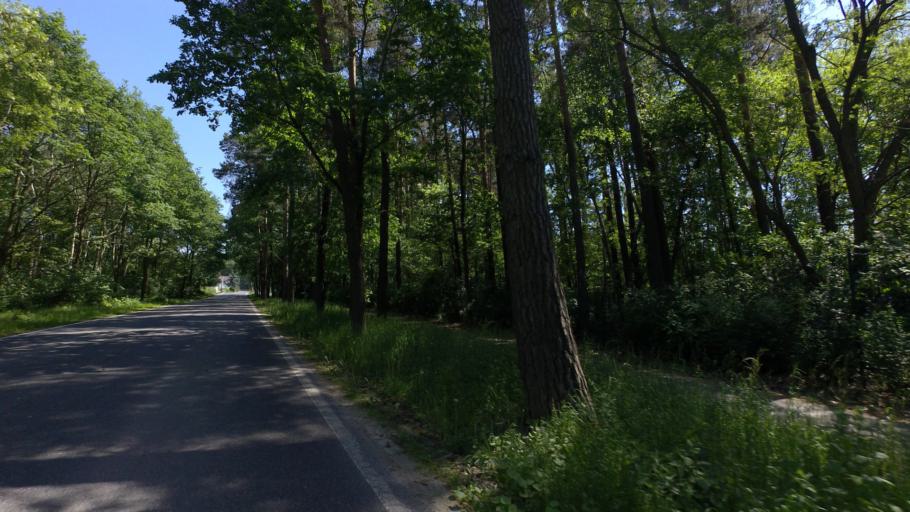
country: DE
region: Brandenburg
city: Cottbus
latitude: 51.7965
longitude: 14.3718
